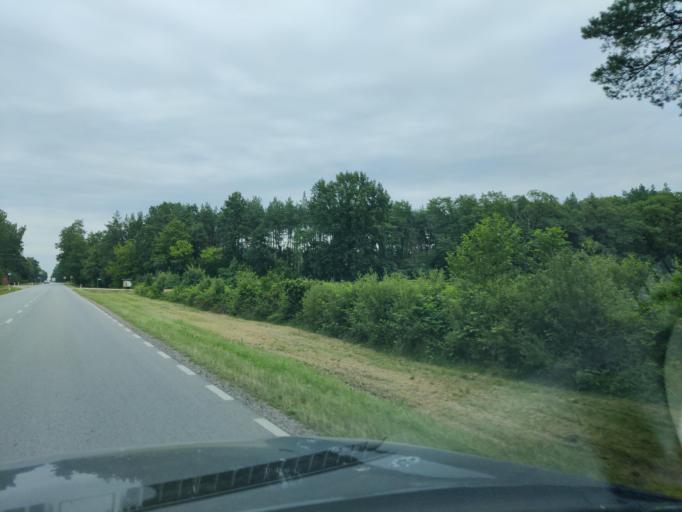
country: PL
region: Masovian Voivodeship
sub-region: Powiat wolominski
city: Strachowka
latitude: 52.3844
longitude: 21.6074
